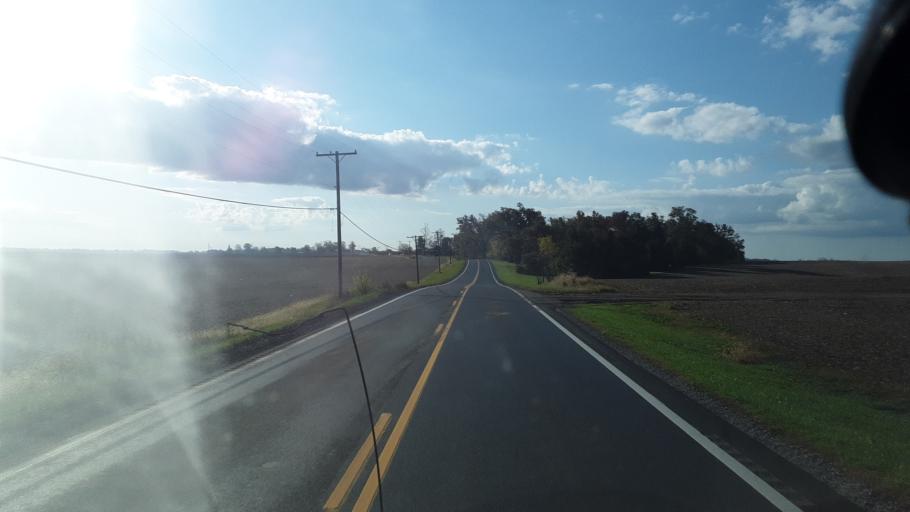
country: US
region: Ohio
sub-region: Fayette County
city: Jeffersonville
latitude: 39.6078
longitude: -83.5244
